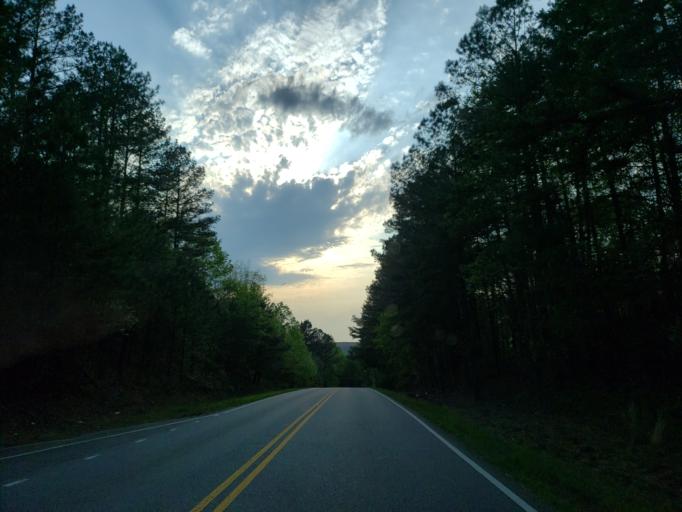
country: US
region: Georgia
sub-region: Cherokee County
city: Ball Ground
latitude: 34.2709
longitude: -84.3690
